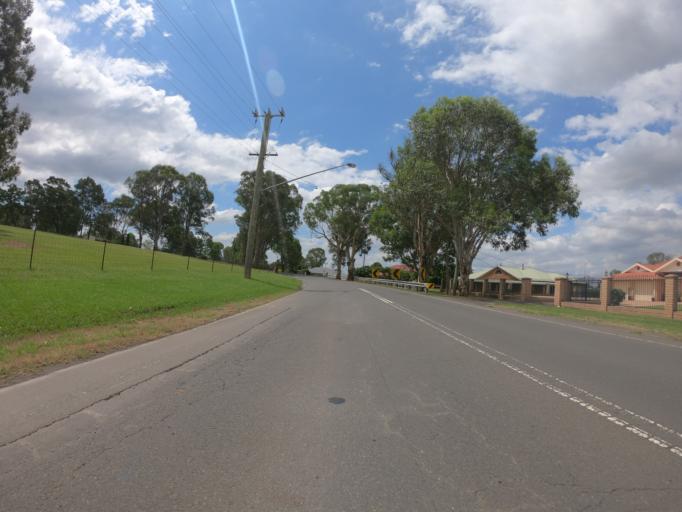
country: AU
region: New South Wales
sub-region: Penrith Municipality
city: Kingswood Park
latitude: -33.8232
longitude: 150.7610
